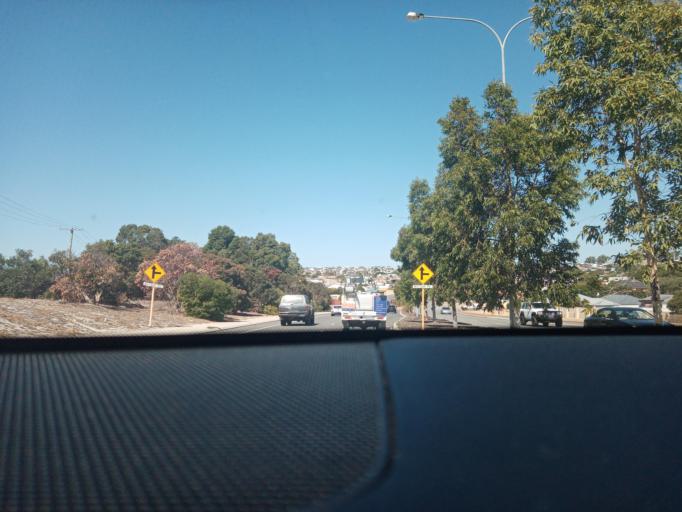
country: AU
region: Western Australia
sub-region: City of Cockburn
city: Beeliar
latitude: -32.1268
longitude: 115.7911
